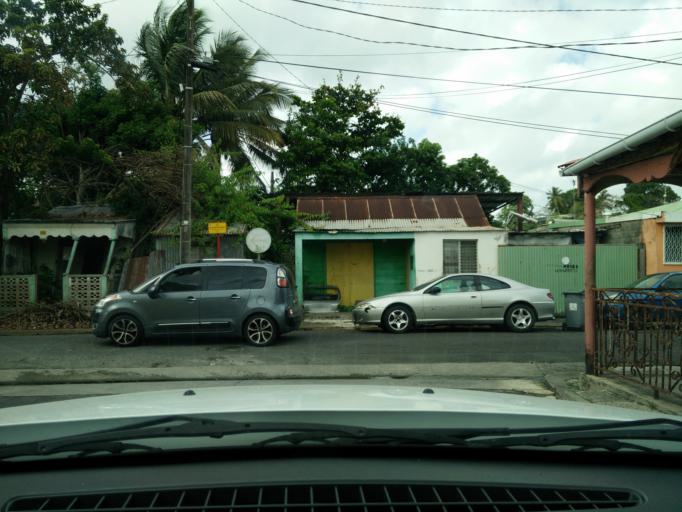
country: GP
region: Guadeloupe
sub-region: Guadeloupe
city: Petit-Canal
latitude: 16.3323
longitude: -61.4593
